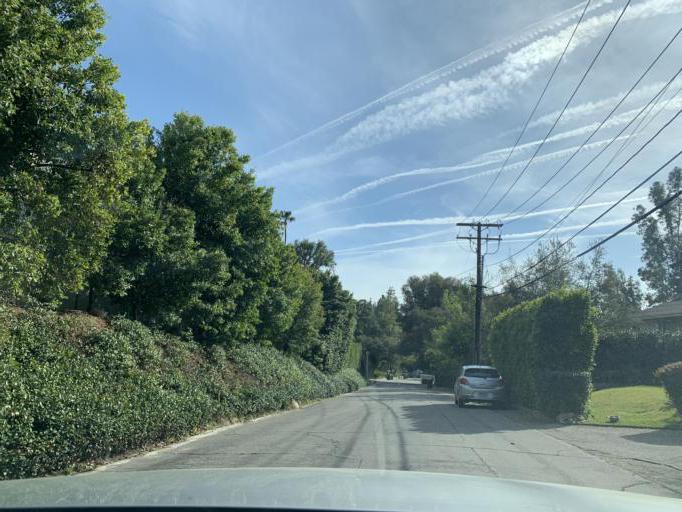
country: US
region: California
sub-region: Los Angeles County
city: South Pasadena
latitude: 34.1319
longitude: -118.1736
